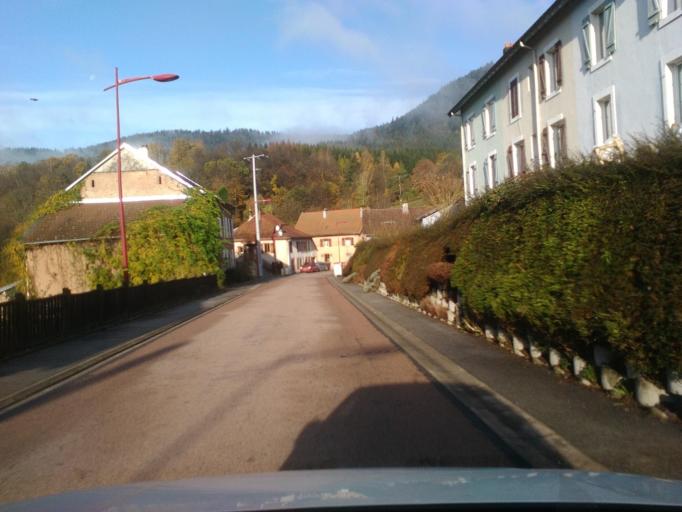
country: FR
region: Lorraine
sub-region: Departement des Vosges
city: Senones
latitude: 48.4299
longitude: 7.0261
